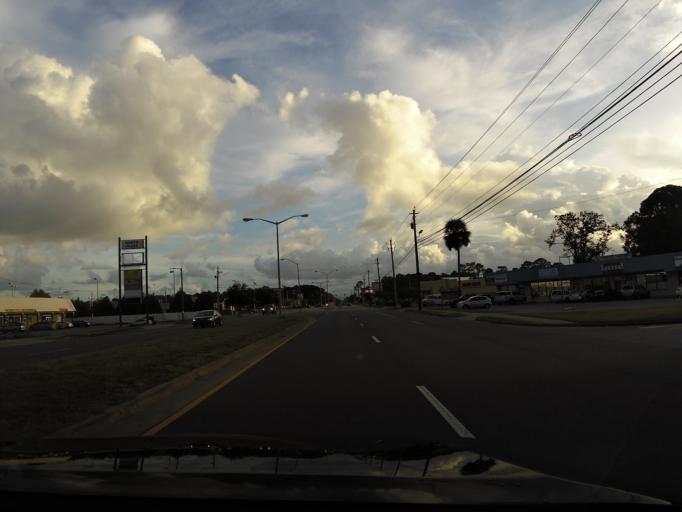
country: US
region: Georgia
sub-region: Glynn County
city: Country Club Estates
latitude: 31.2062
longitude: -81.4826
